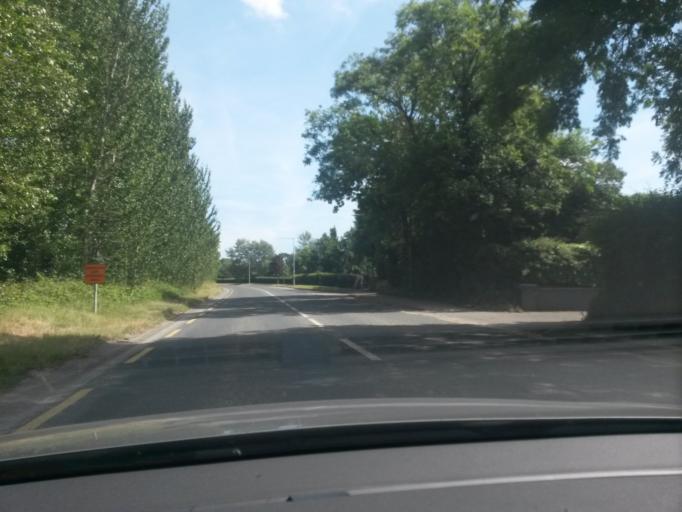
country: IE
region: Leinster
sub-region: Kildare
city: Naas
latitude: 53.2115
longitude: -6.6467
